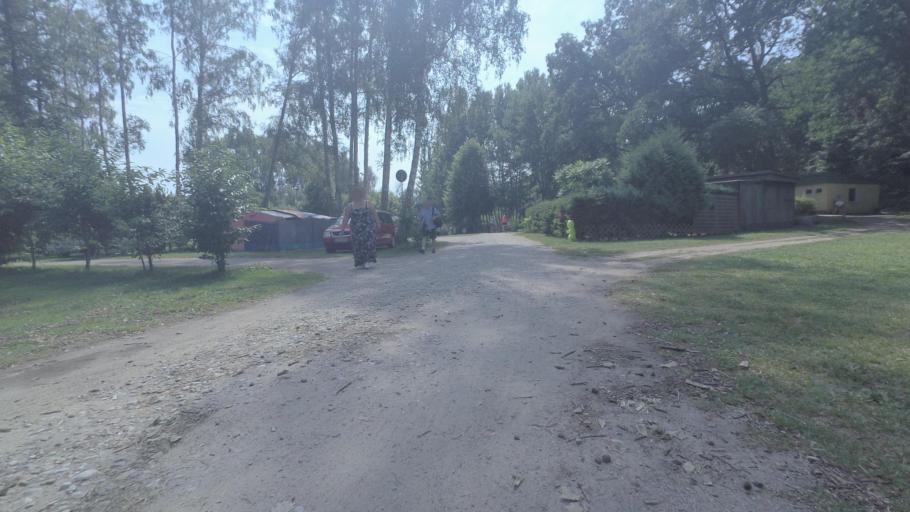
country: DE
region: Mecklenburg-Vorpommern
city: Waren
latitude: 53.5091
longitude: 12.6466
